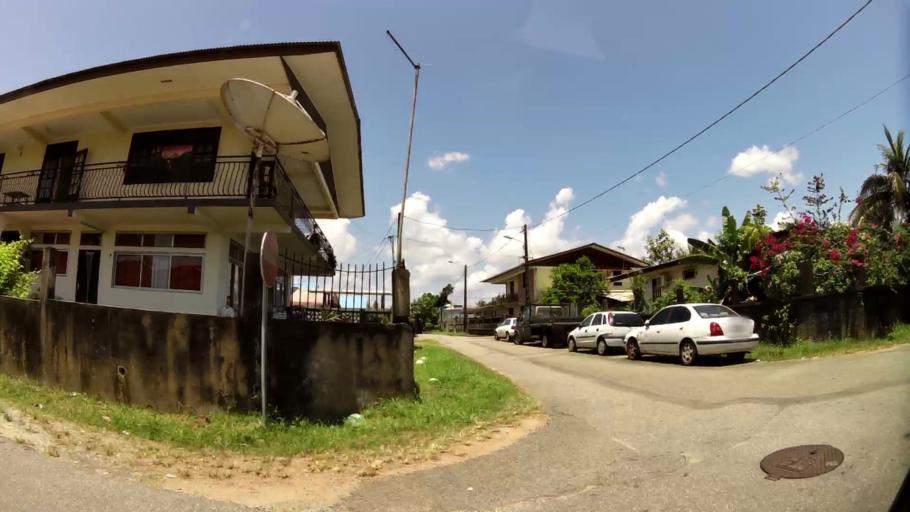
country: GF
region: Guyane
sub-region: Guyane
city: Matoury
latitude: 4.8870
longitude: -52.3391
